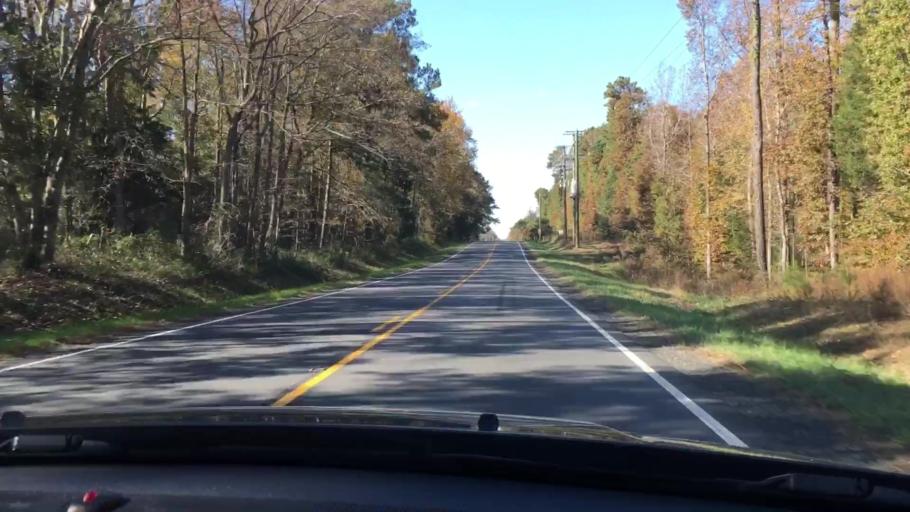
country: US
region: Virginia
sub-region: King William County
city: King William
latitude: 37.7007
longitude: -77.0426
